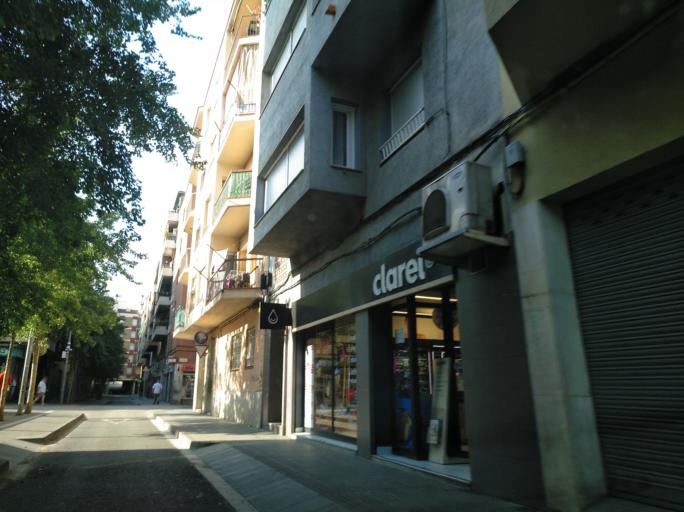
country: ES
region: Catalonia
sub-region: Provincia de Girona
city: Salt
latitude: 41.9730
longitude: 2.7908
